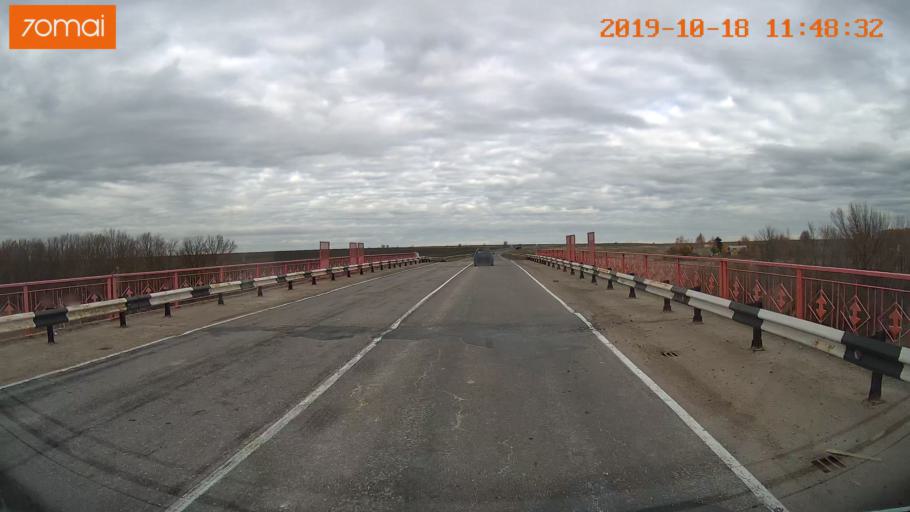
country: RU
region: Rjazan
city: Mikhaylov
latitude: 54.2403
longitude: 38.9836
